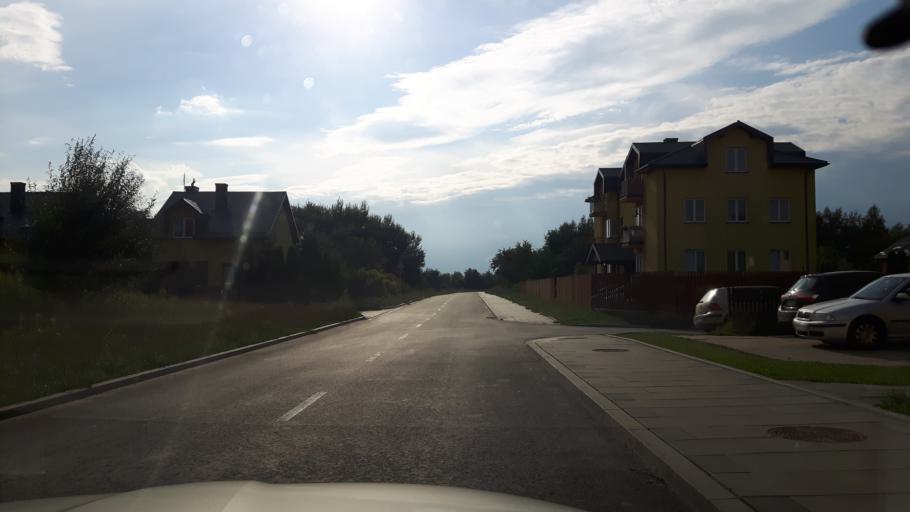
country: PL
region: Masovian Voivodeship
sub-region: Powiat wolominski
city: Marki
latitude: 52.3254
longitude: 21.0888
